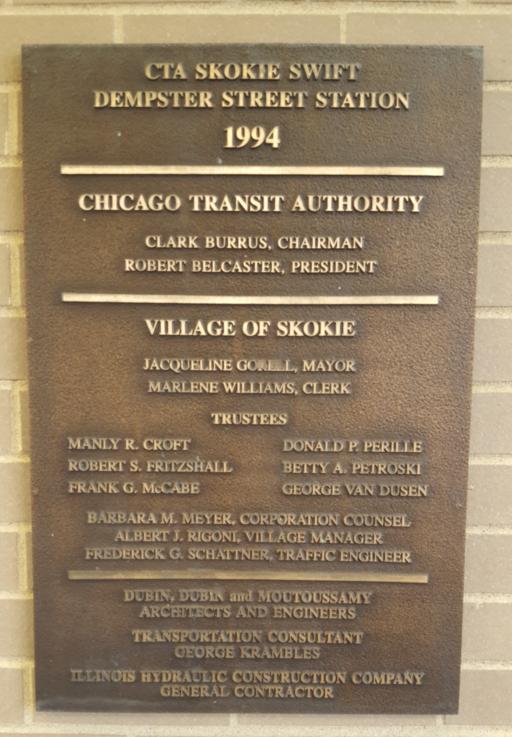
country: US
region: Illinois
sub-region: Cook County
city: Skokie
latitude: 42.0389
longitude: -87.7519
